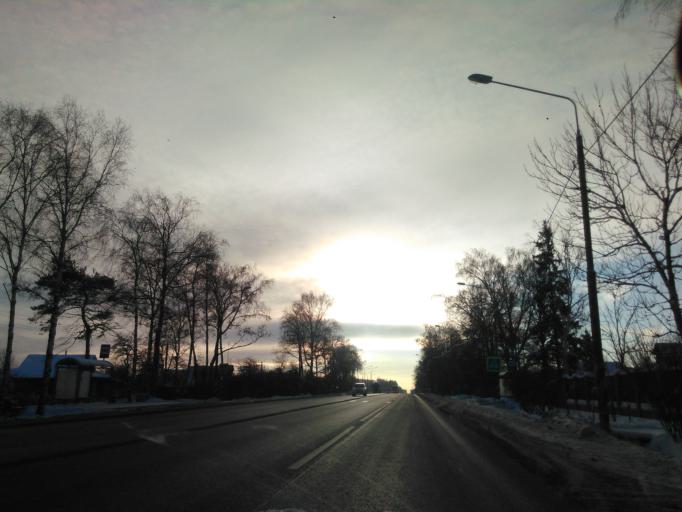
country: RU
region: Moskovskaya
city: Spas-Zaulok
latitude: 56.4679
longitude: 36.5844
